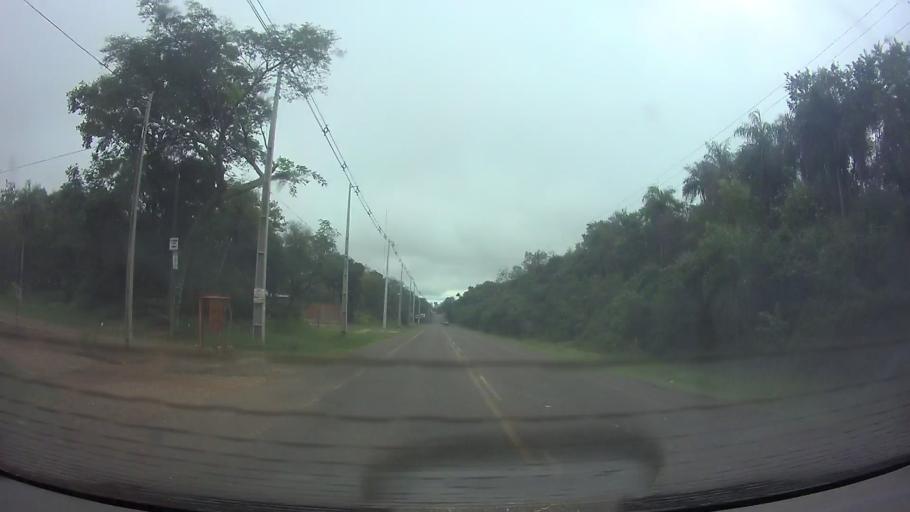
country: PY
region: Cordillera
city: Altos
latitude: -25.2803
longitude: -57.2617
